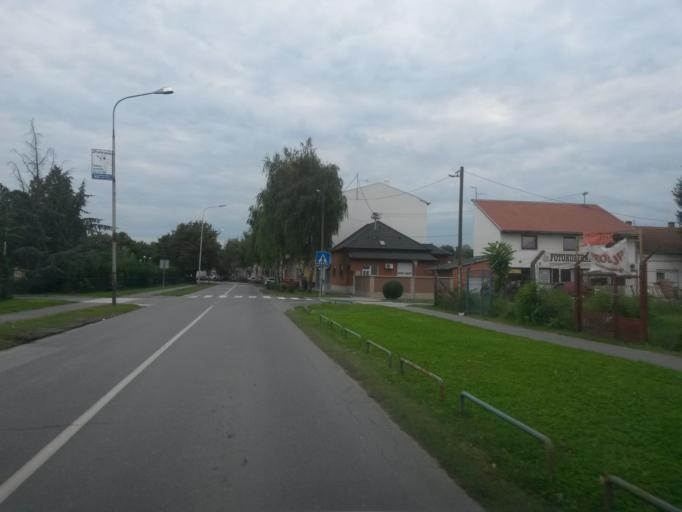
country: HR
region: Osjecko-Baranjska
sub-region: Grad Osijek
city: Osijek
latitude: 45.5506
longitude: 18.6905
